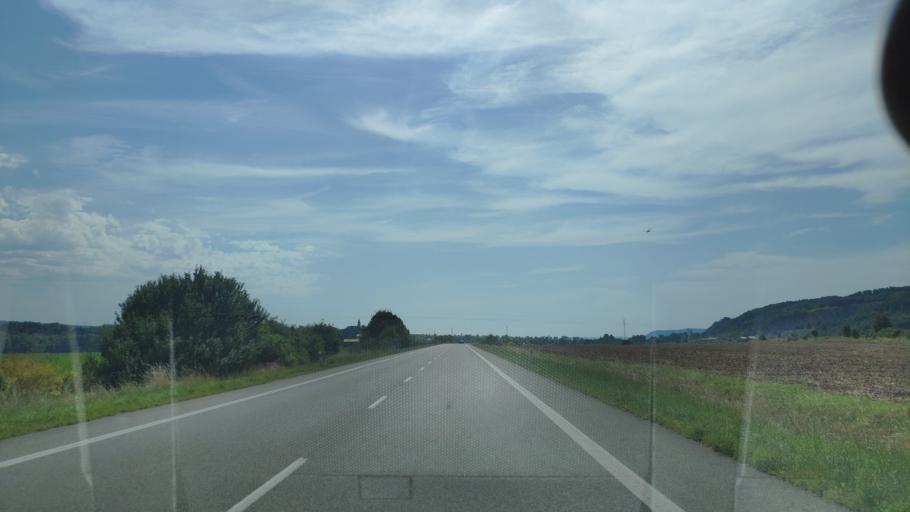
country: HU
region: Borsod-Abauj-Zemplen
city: Putnok
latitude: 48.5093
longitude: 20.3805
